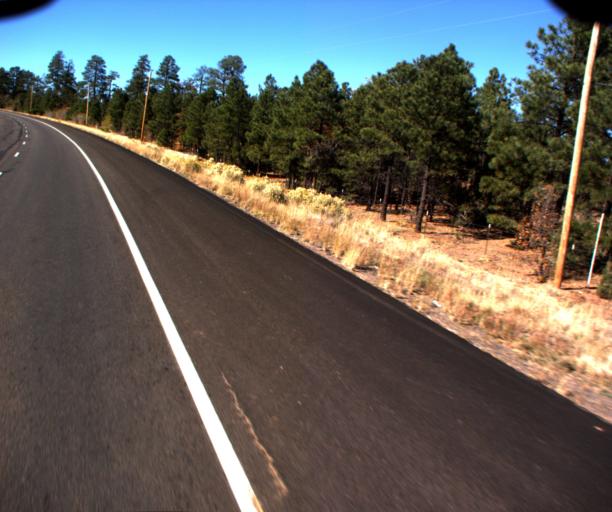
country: US
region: Arizona
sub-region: Apache County
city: Saint Michaels
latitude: 35.6706
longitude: -109.1669
